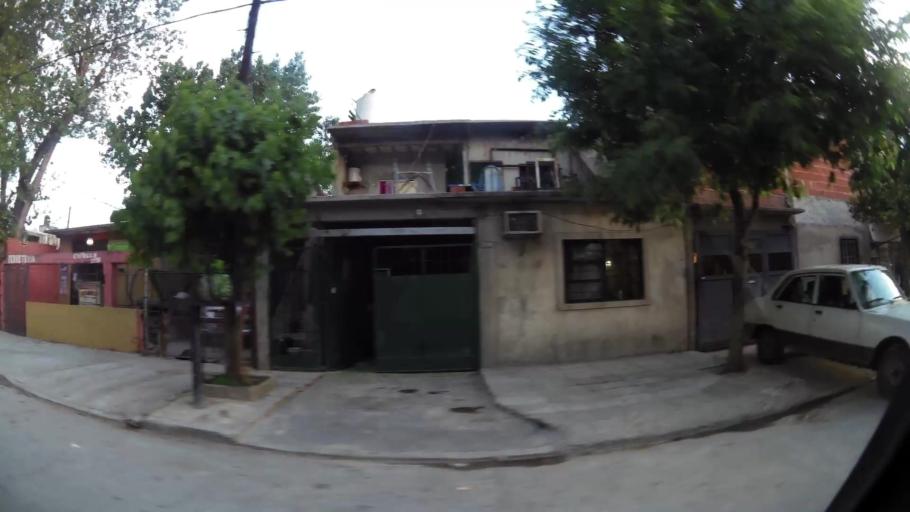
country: AR
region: Buenos Aires
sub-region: Partido de Avellaneda
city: Avellaneda
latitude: -34.6814
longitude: -58.3253
